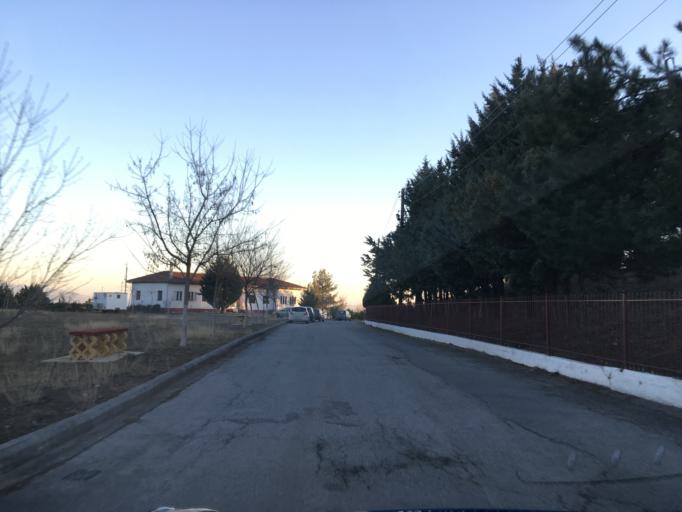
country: GR
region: West Macedonia
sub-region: Nomos Kozanis
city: Koila
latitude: 40.3236
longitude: 21.8220
